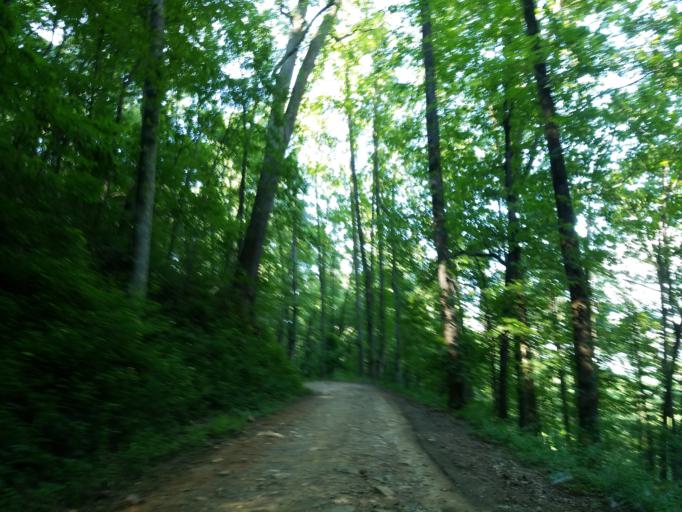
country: US
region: Georgia
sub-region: Dawson County
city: Dawsonville
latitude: 34.5906
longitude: -84.2052
